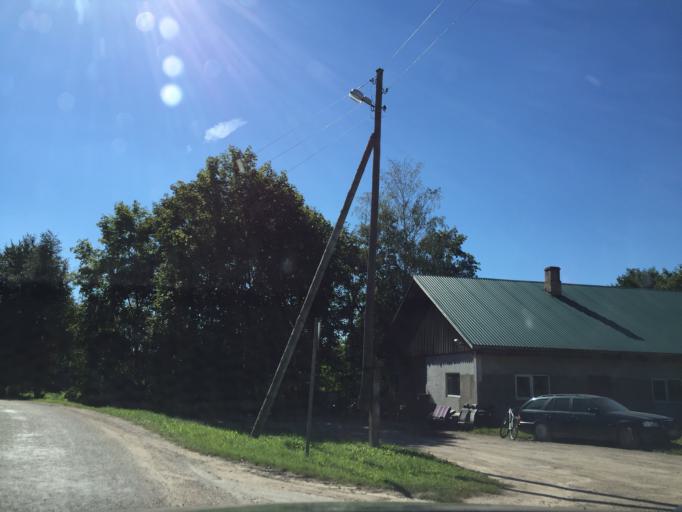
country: LV
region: Akniste
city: Akniste
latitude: 56.1579
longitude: 25.7409
